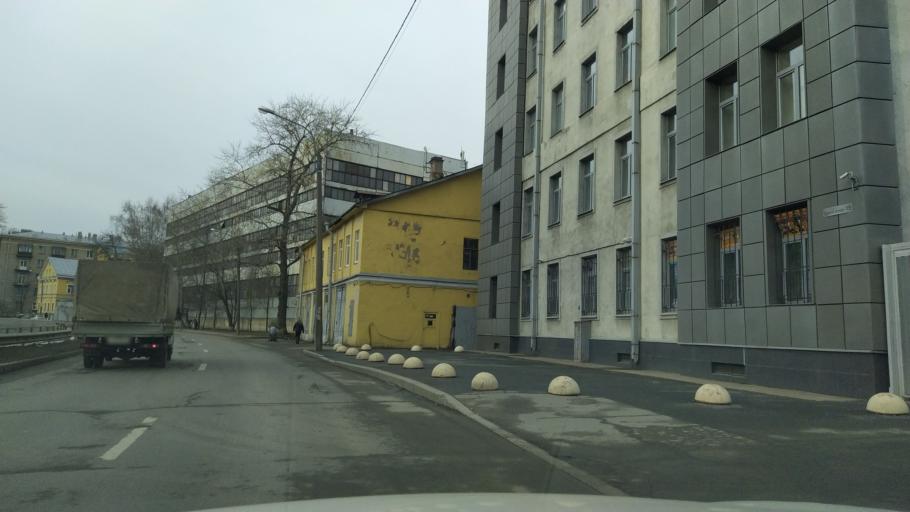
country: RU
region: Leningrad
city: Chernaya Rechka
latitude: 59.9845
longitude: 30.3167
